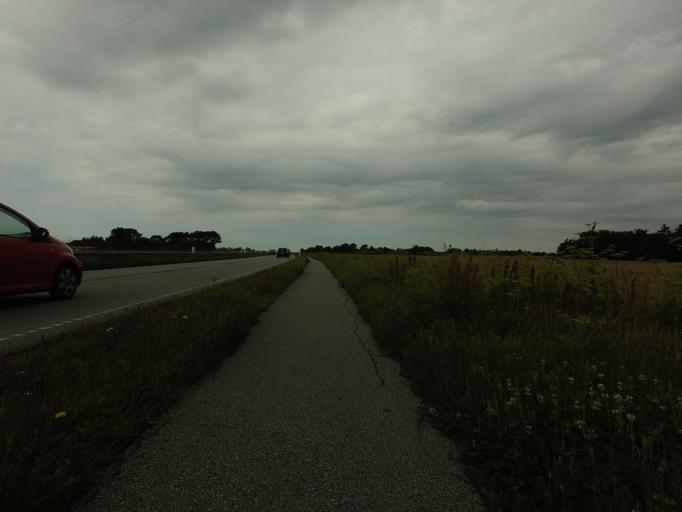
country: DK
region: North Denmark
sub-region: Alborg Kommune
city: Vadum
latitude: 57.1057
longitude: 9.8806
